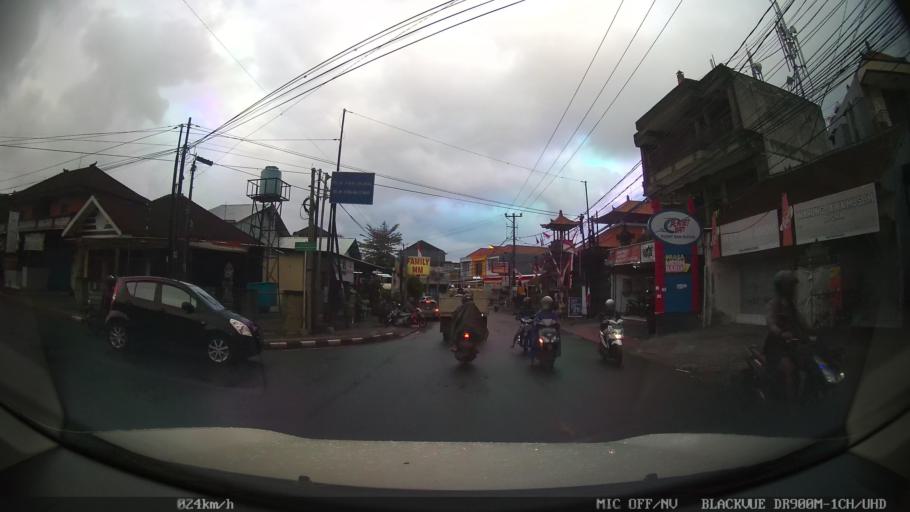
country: ID
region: Bali
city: Banjar Kayangan
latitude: -8.6249
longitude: 115.2239
